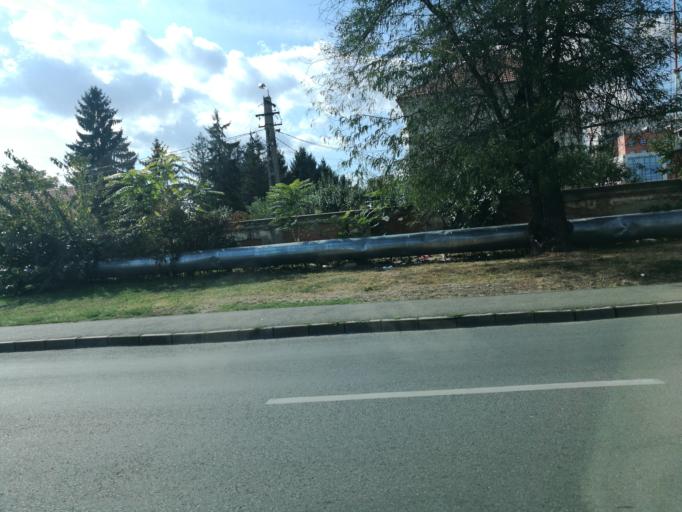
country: RO
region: Bihor
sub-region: Comuna Biharea
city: Oradea
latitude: 47.0556
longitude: 21.9177
